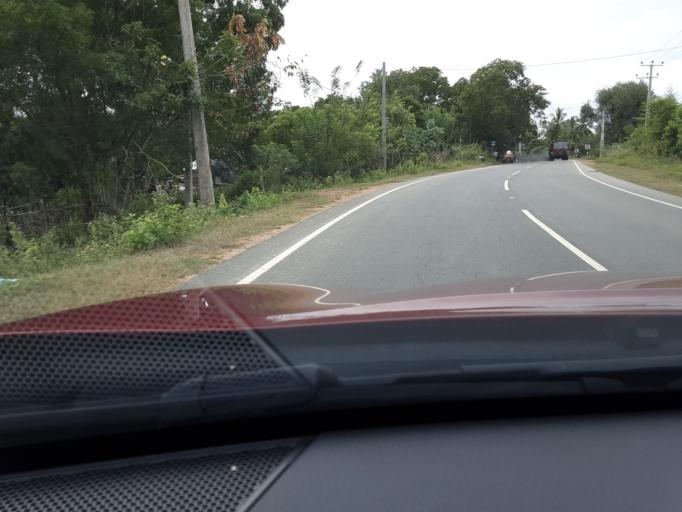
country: LK
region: Eastern Province
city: Eravur Town
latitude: 7.6869
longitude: 81.5127
